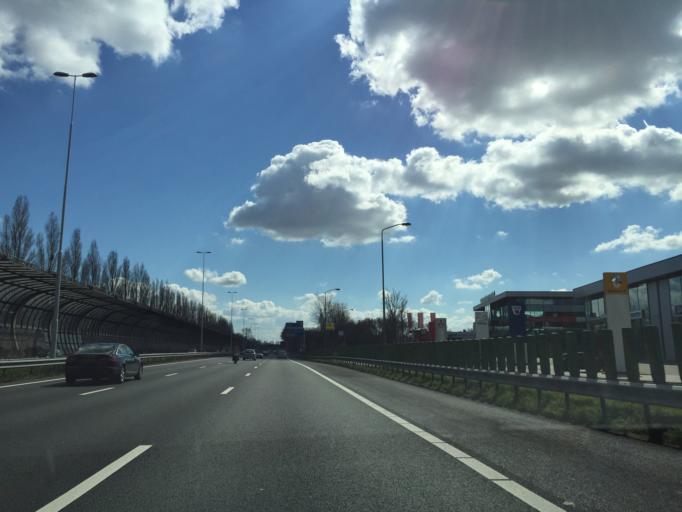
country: NL
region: South Holland
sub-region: Gemeente Zwijndrecht
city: Zwijndrecht
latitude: 51.7908
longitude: 4.6490
